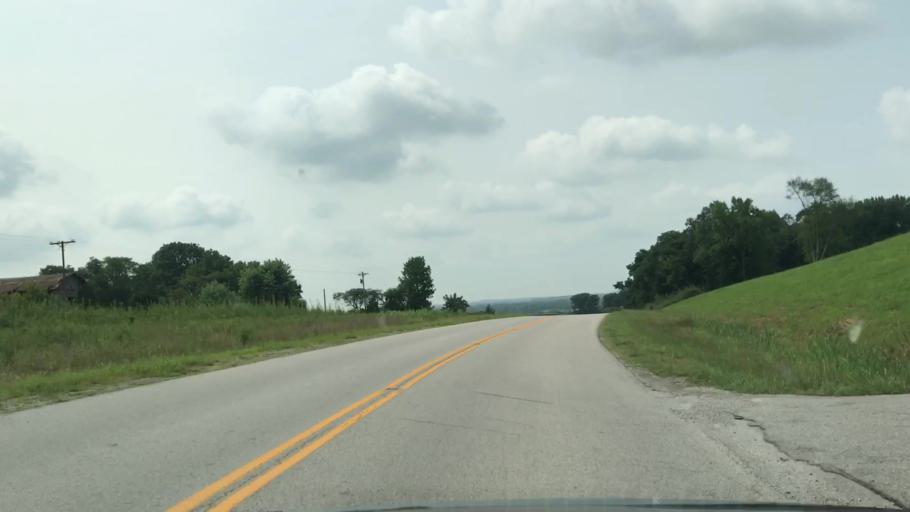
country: US
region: Kentucky
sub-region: Edmonson County
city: Brownsville
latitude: 37.1058
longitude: -86.1460
